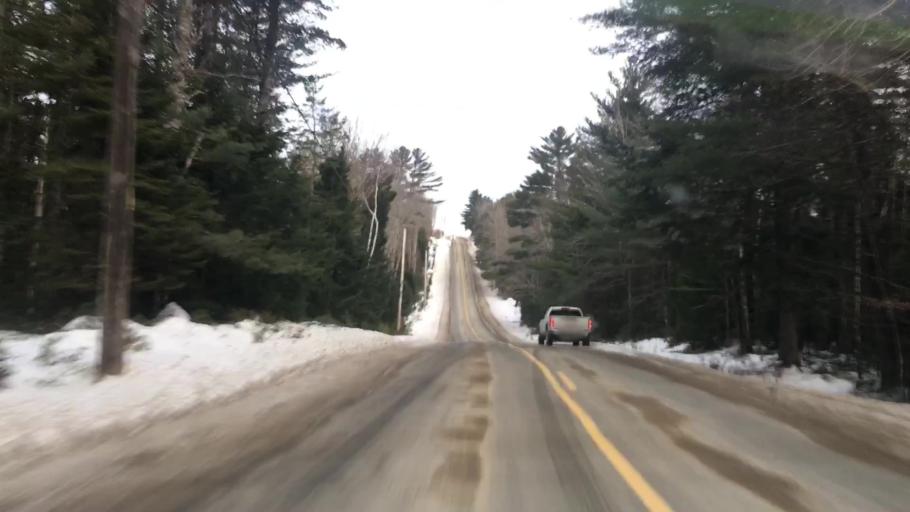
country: US
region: Maine
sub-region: Hancock County
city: Franklin
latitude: 44.8407
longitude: -68.3242
